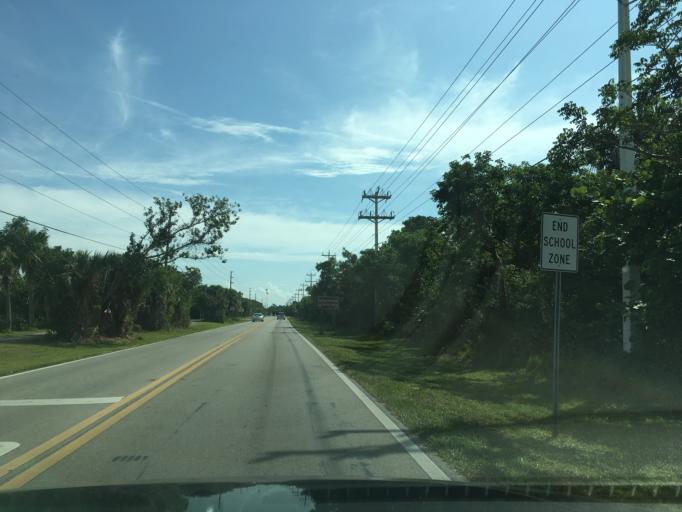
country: US
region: Florida
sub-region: Lee County
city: Saint James City
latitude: 26.4456
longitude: -82.1150
